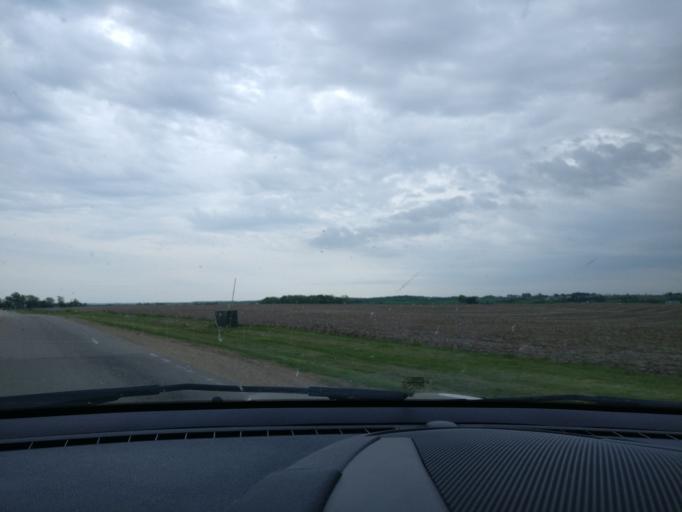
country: US
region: Wisconsin
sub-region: Lafayette County
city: Darlington
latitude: 42.7526
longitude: -90.0117
